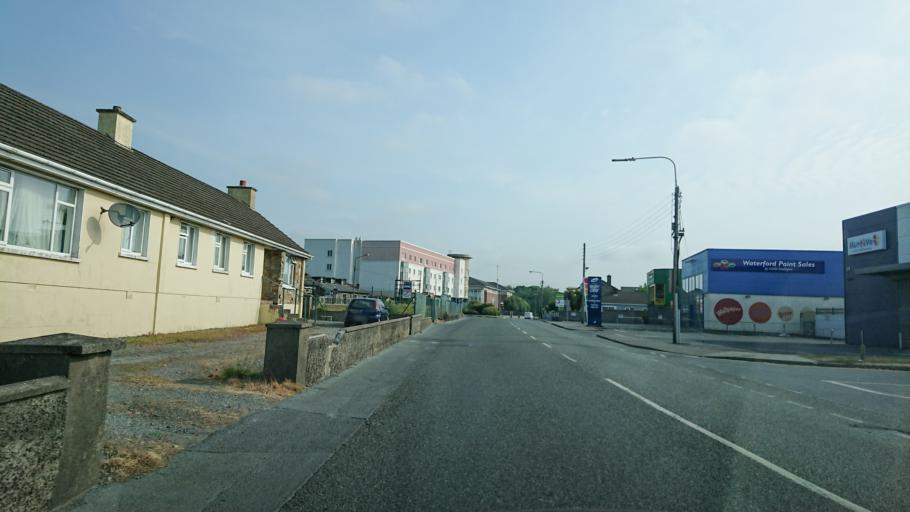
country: IE
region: Munster
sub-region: Waterford
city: Waterford
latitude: 52.2504
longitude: -7.1179
